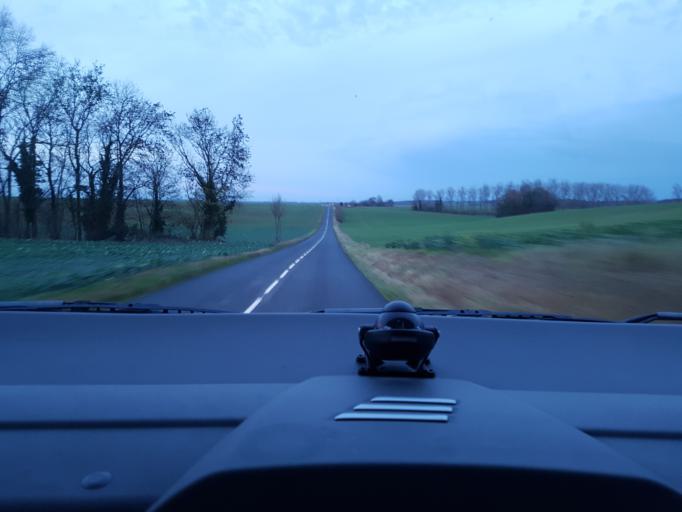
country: FR
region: Picardie
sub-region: Departement de la Somme
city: Beauquesne
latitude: 50.0772
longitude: 2.4235
